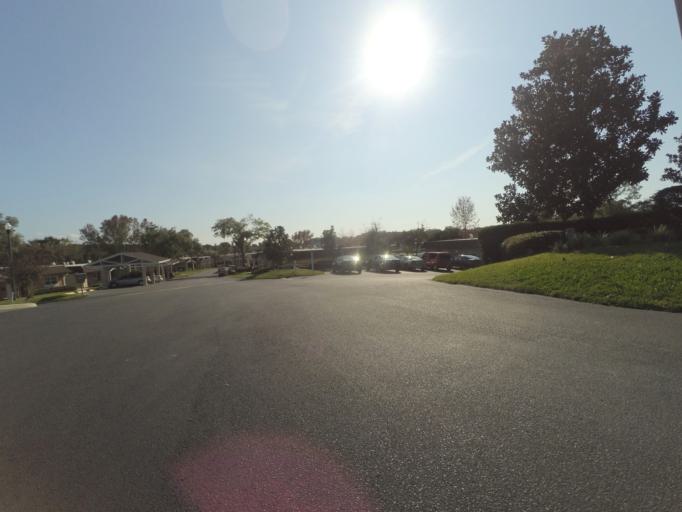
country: US
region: Florida
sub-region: Lake County
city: Umatilla
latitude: 28.9671
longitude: -81.6538
